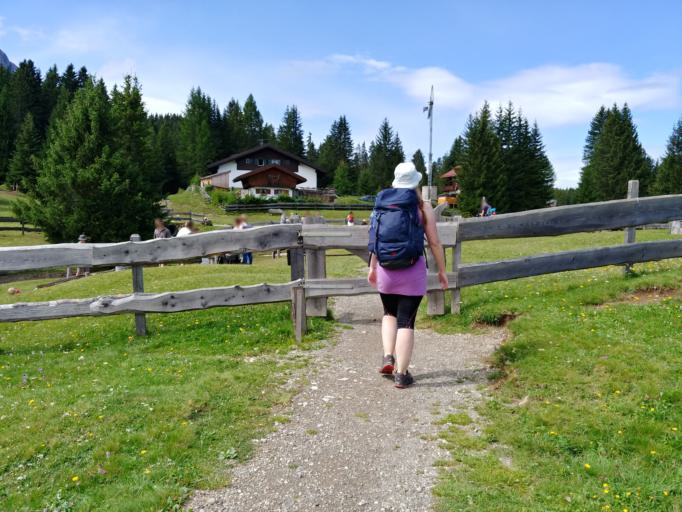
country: IT
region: Trentino-Alto Adige
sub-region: Bolzano
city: Santa Cristina Valgardena
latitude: 46.5484
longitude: 11.7209
